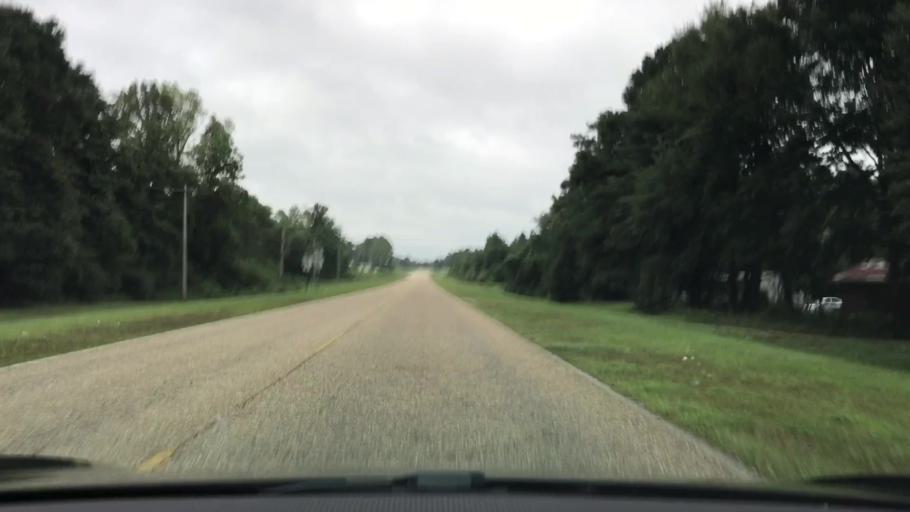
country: US
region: Alabama
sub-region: Coffee County
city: Elba
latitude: 31.4075
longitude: -86.0825
